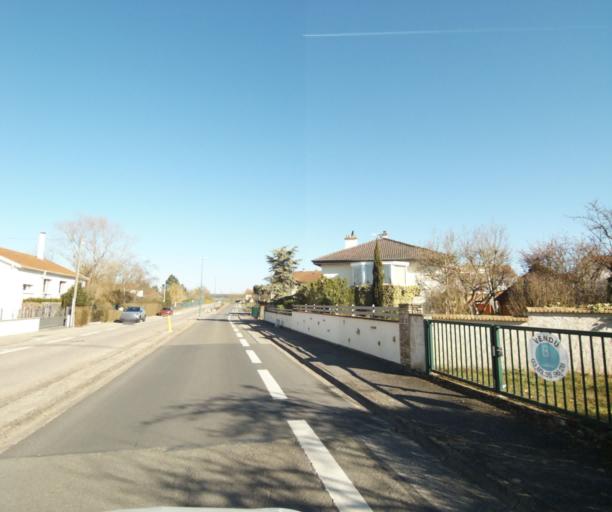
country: FR
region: Lorraine
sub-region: Departement de Meurthe-et-Moselle
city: Saulxures-les-Nancy
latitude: 48.6790
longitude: 6.2413
